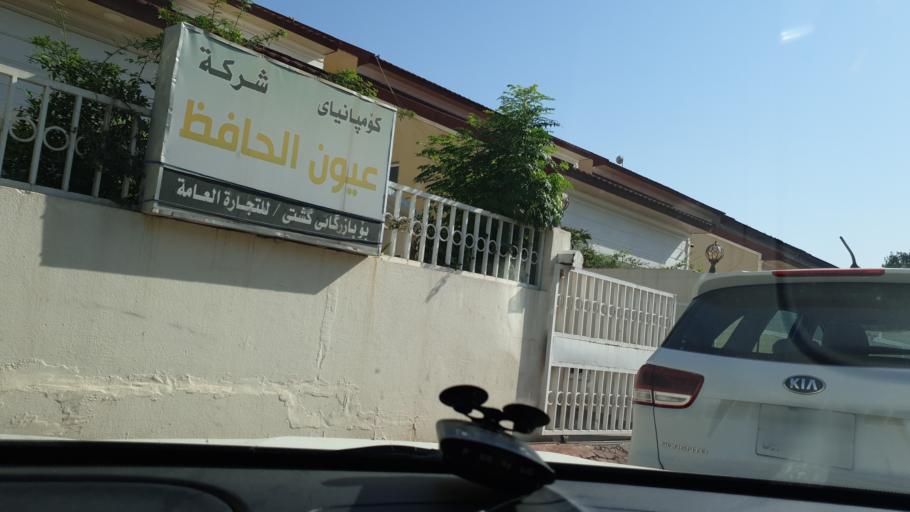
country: IQ
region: Arbil
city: Erbil
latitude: 36.1866
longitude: 43.9700
